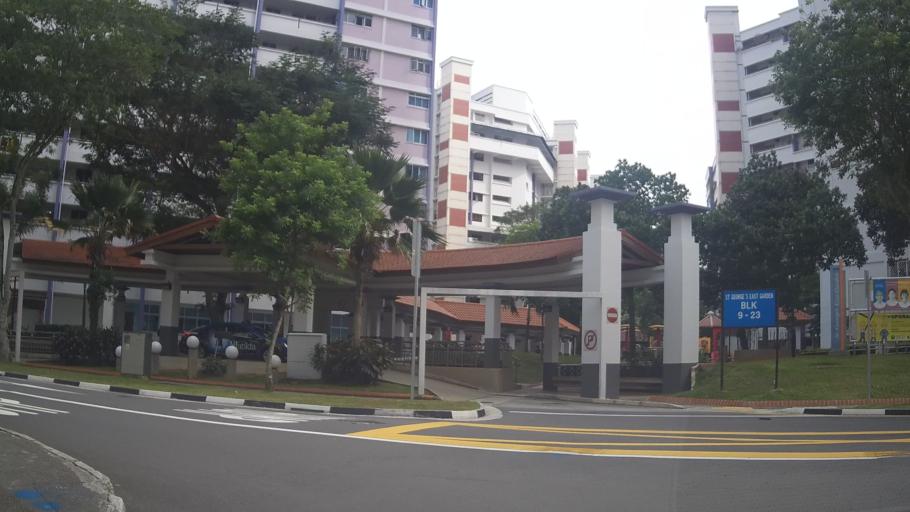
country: SG
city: Singapore
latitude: 1.3226
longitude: 103.8619
